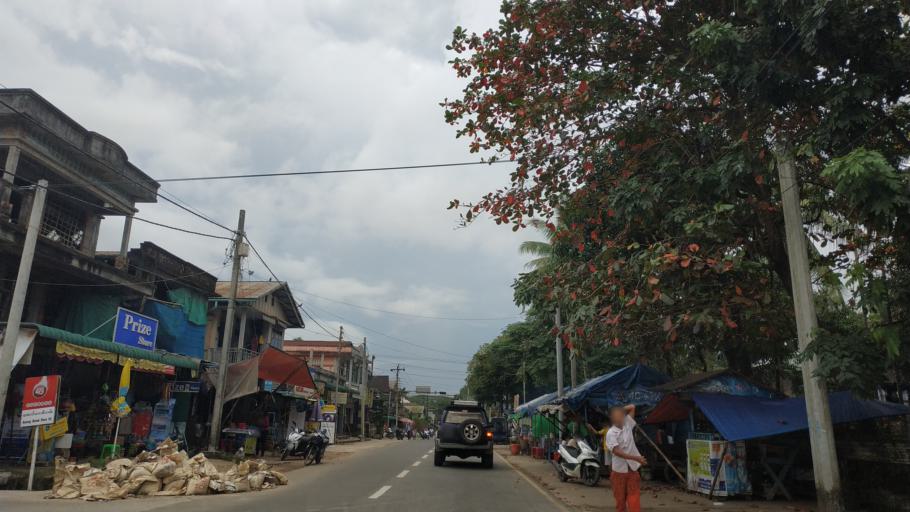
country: MM
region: Tanintharyi
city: Dawei
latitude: 14.0765
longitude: 98.1971
